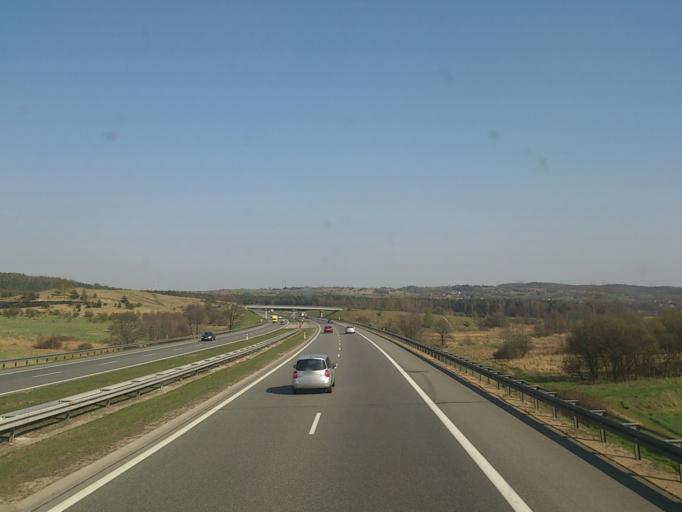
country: PL
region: Lesser Poland Voivodeship
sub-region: Powiat chrzanowski
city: Grojec
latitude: 50.0917
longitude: 19.5754
